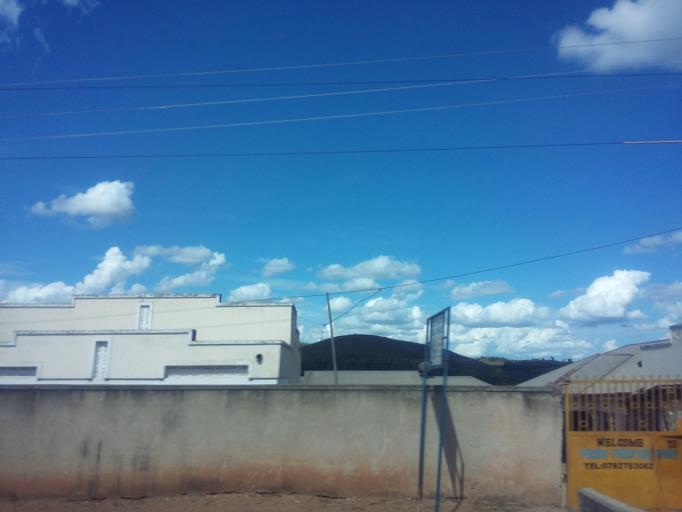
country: UG
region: Western Region
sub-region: Ntungamo District
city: Ntungamo
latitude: -0.9617
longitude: 30.2054
